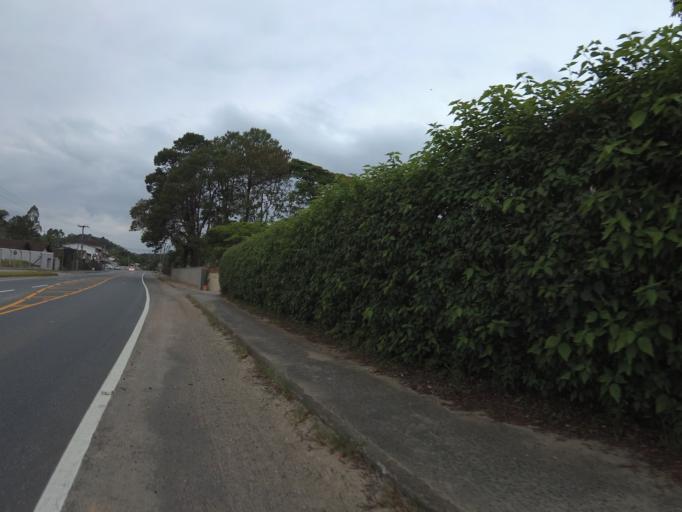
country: BR
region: Santa Catarina
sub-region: Indaial
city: Indaial
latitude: -26.8453
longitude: -49.1584
